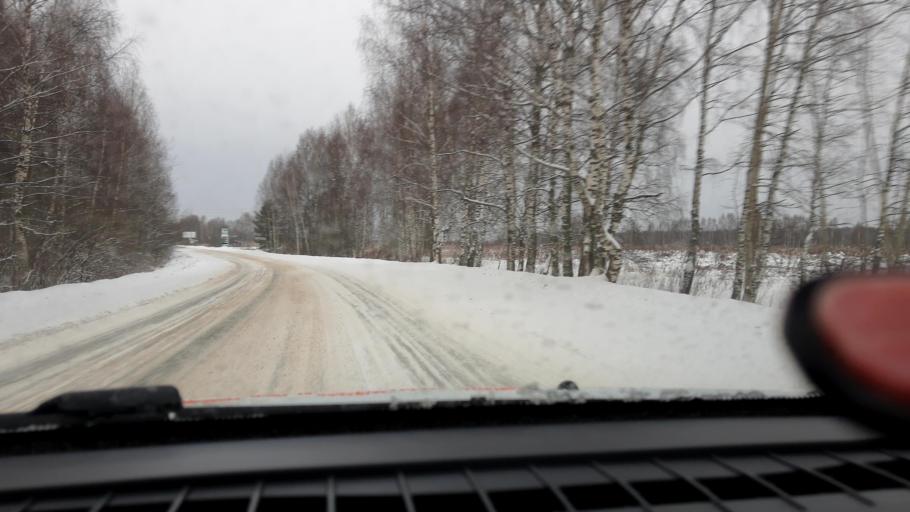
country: RU
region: Nizjnij Novgorod
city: Pamyat' Parizhskoy Kommuny
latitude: 56.2645
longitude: 44.4403
